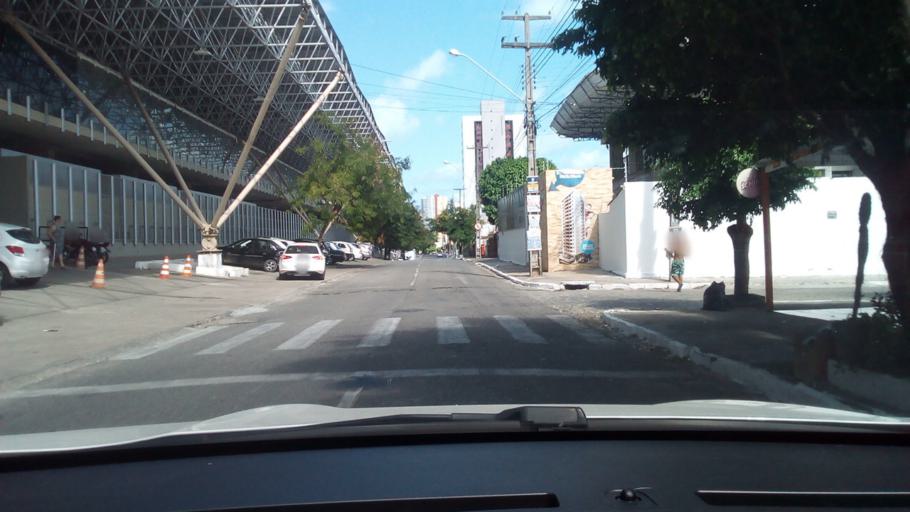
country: BR
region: Paraiba
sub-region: Joao Pessoa
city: Joao Pessoa
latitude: -7.1229
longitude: -34.8434
